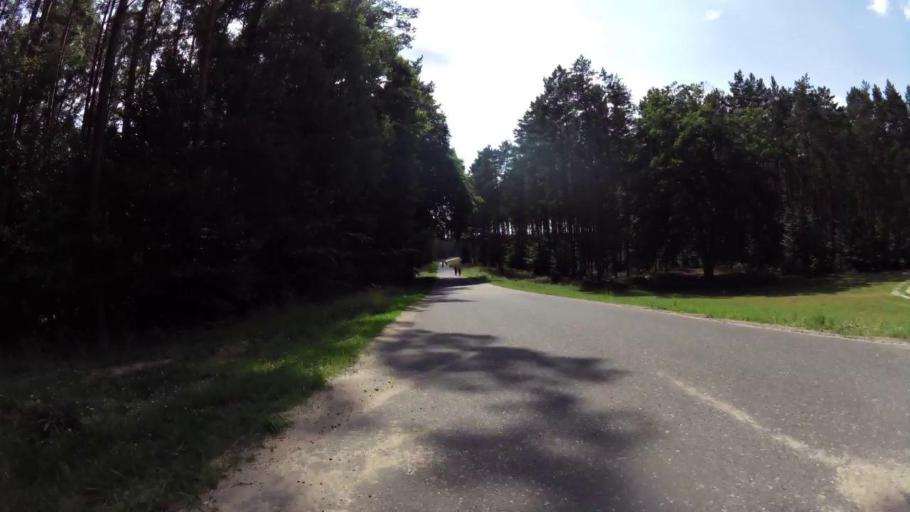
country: PL
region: West Pomeranian Voivodeship
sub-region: Powiat choszczenski
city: Drawno
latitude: 53.3689
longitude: 15.7218
